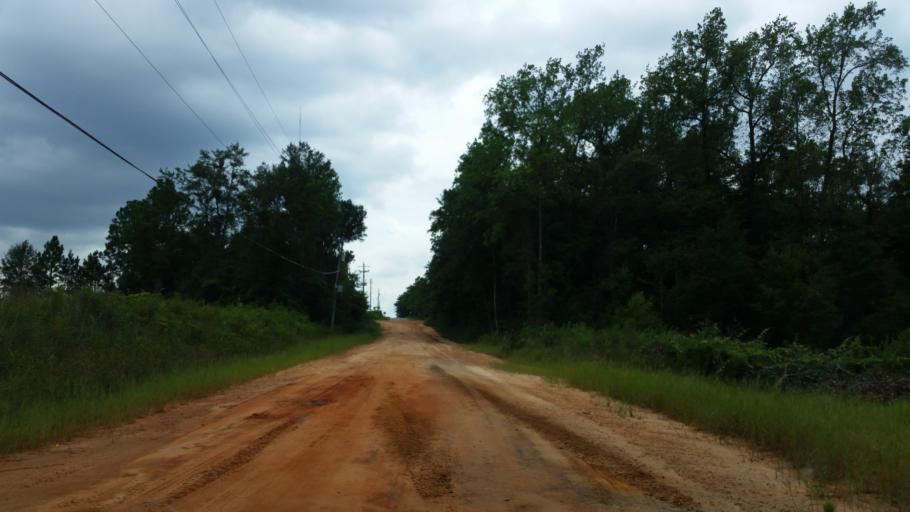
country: US
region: Florida
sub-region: Escambia County
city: Molino
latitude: 30.7181
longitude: -87.4047
